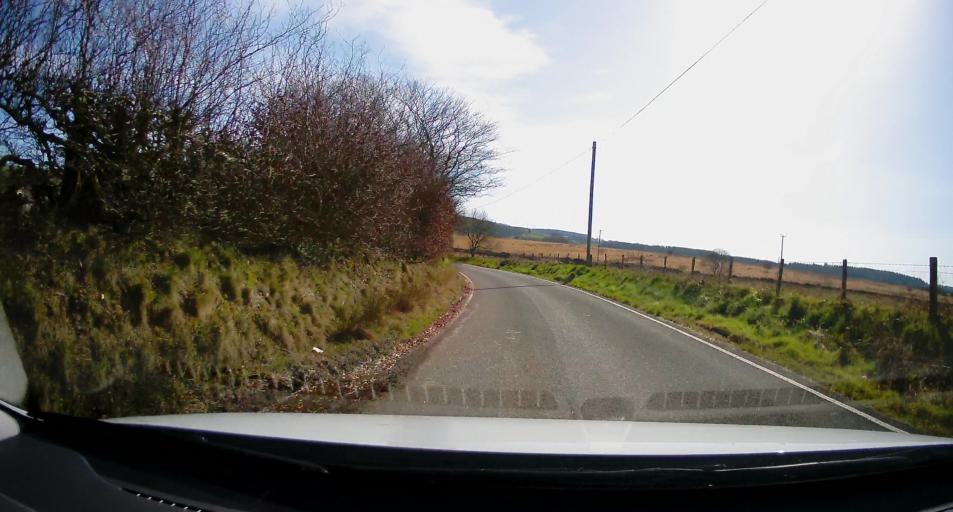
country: GB
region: Wales
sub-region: County of Ceredigion
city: Lledrod
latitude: 52.2878
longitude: -4.0666
